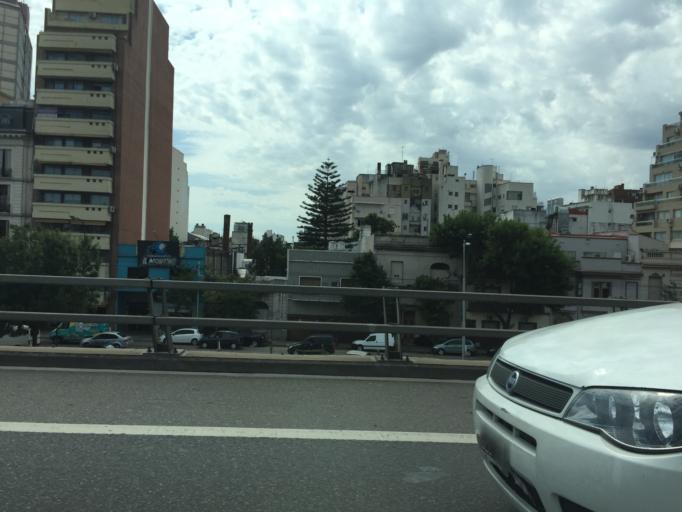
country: AR
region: Buenos Aires
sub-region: Partido de Avellaneda
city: Avellaneda
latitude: -34.6401
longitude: -58.3763
